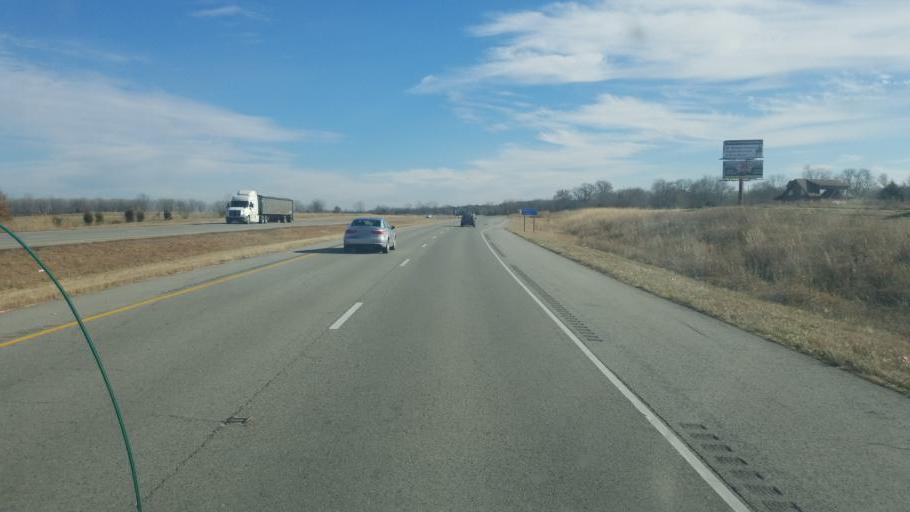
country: US
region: Illinois
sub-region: Williamson County
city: Marion
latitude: 37.7319
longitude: -88.7913
